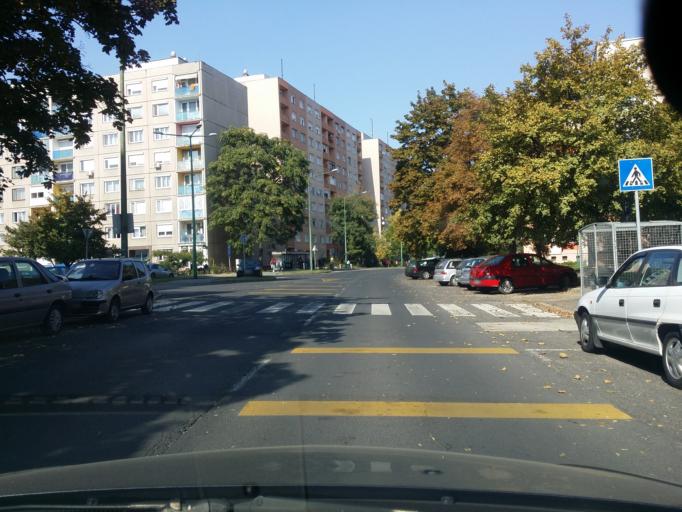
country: HU
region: Fejer
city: dunaujvaros
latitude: 46.9709
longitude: 18.9331
